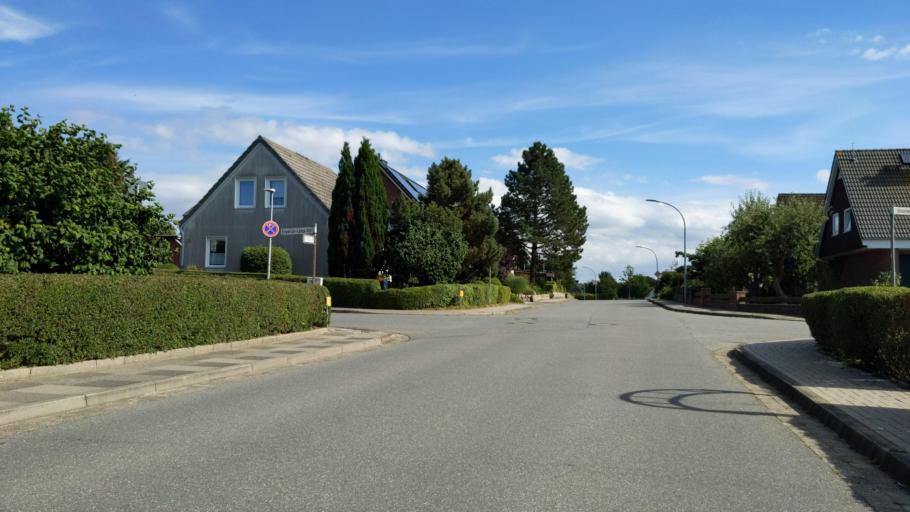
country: DE
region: Schleswig-Holstein
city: Ascheberg
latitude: 54.1517
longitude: 10.3405
